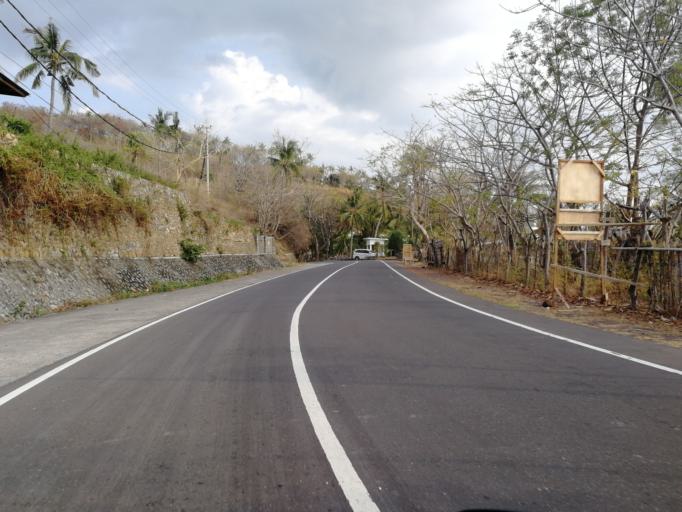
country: ID
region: West Nusa Tenggara
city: Karangsubagan
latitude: -8.4440
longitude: 116.0339
